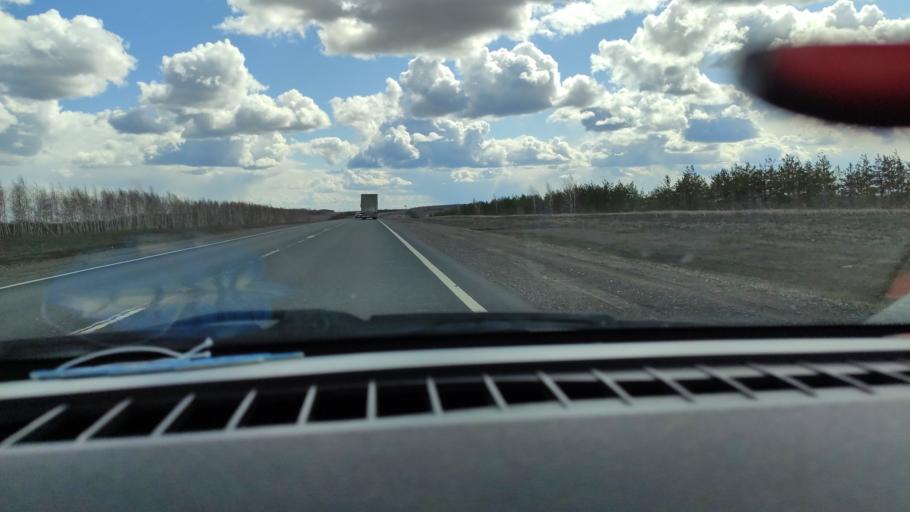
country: RU
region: Samara
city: Syzran'
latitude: 52.8887
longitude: 48.2941
